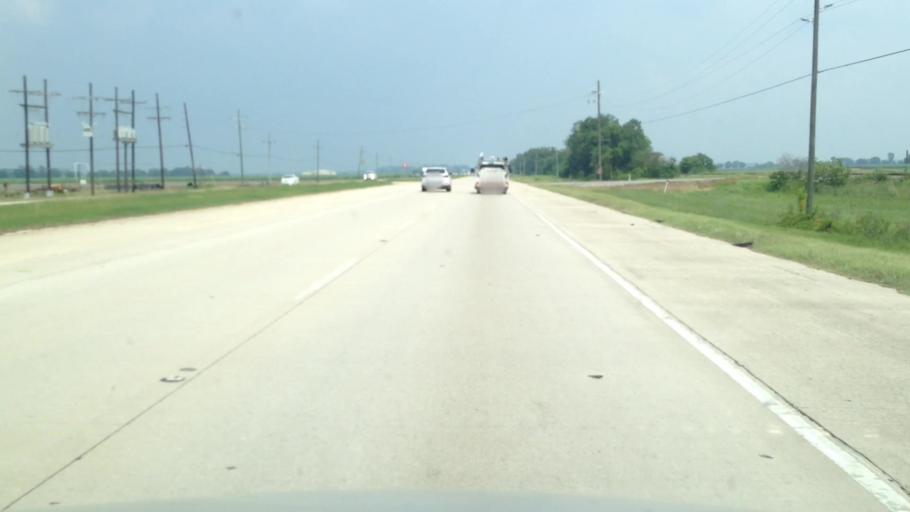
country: US
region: Louisiana
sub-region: West Baton Rouge Parish
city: Port Allen
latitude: 30.4973
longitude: -91.3022
